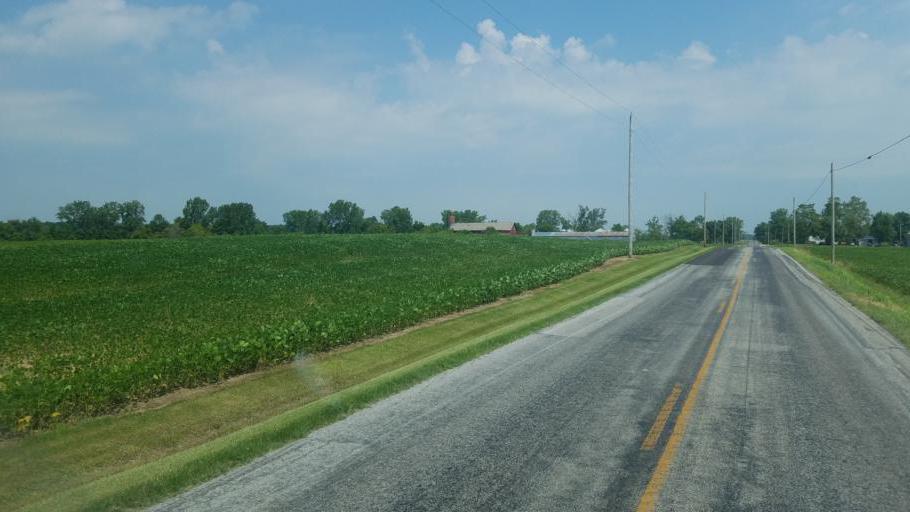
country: US
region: Ohio
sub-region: Union County
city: Richwood
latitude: 40.5544
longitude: -83.3909
